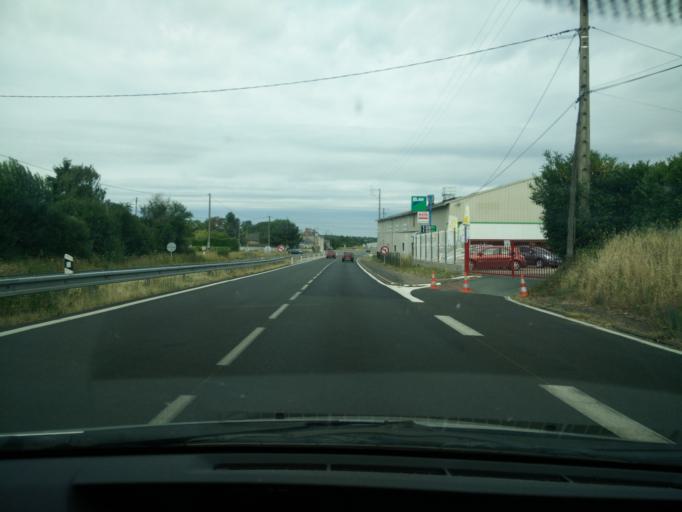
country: FR
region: Pays de la Loire
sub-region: Departement de Maine-et-Loire
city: Saint-Melaine-sur-Aubance
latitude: 47.3873
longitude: -0.4916
